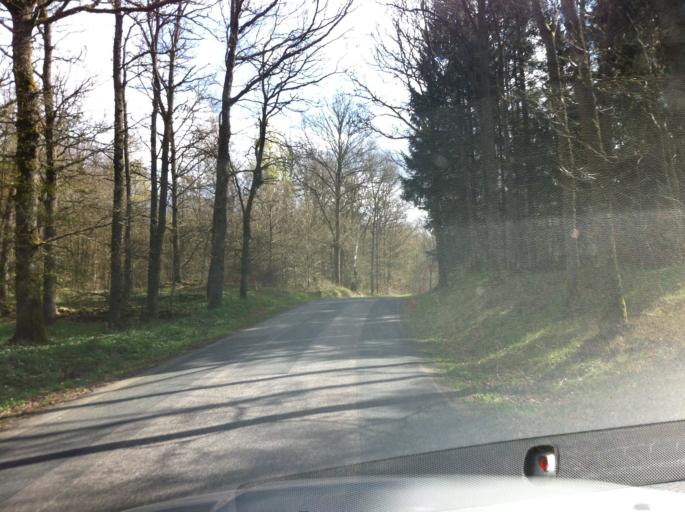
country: SE
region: Skane
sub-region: Hoors Kommun
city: Satofta
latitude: 55.9130
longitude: 13.6109
